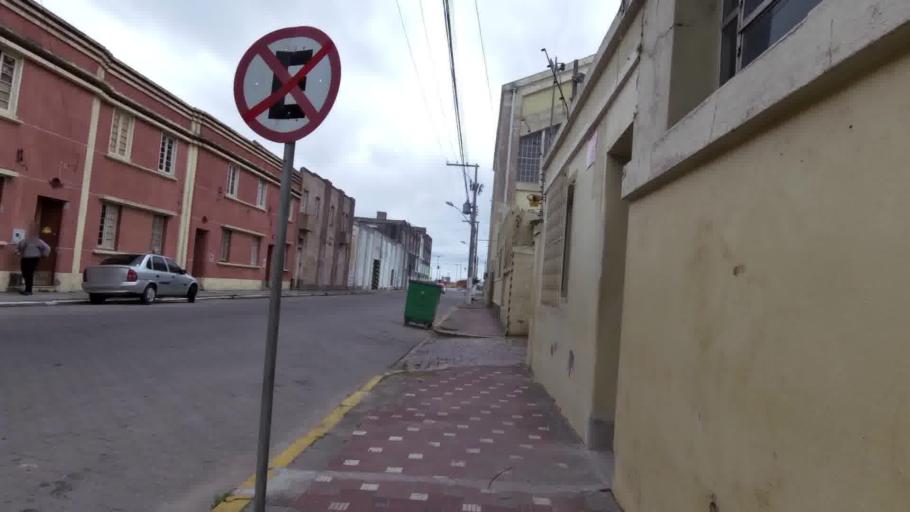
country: BR
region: Rio Grande do Sul
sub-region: Rio Grande
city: Rio Grande
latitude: -32.0297
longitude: -52.1003
